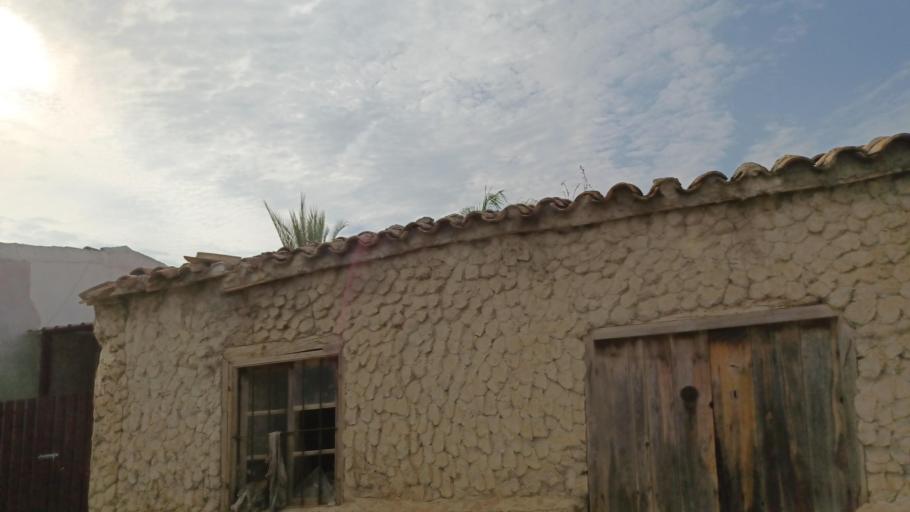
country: CY
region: Lefkosia
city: Peristerona
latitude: 35.1013
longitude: 33.0943
